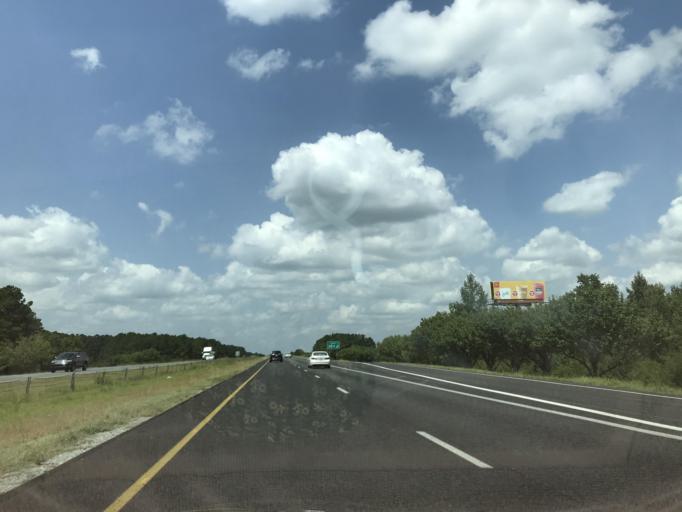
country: US
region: North Carolina
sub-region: Duplin County
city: Wallace
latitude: 34.7664
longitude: -77.9618
